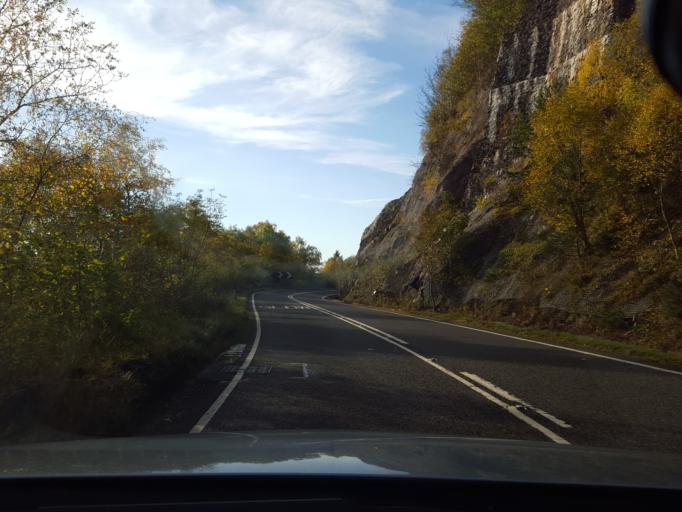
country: GB
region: Scotland
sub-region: Highland
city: Beauly
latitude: 57.3176
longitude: -4.4513
